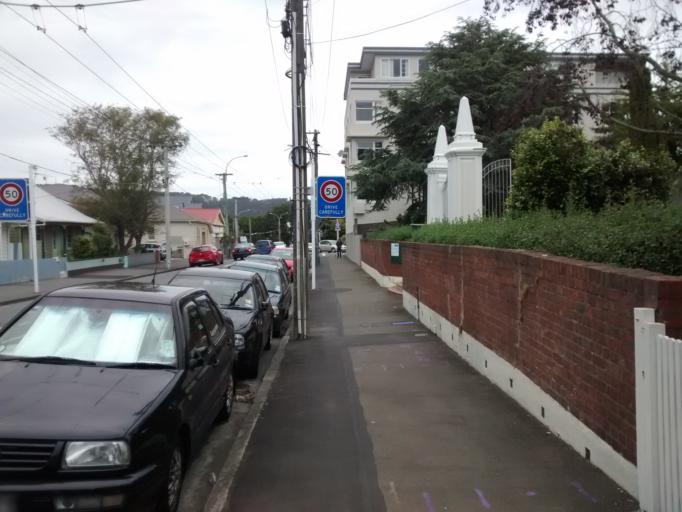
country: NZ
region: Wellington
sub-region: Wellington City
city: Wellington
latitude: -41.2957
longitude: 174.7688
